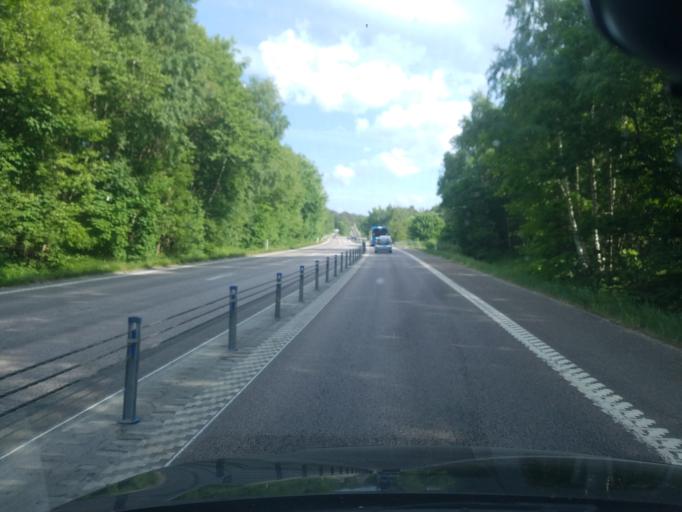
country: SE
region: Vaestra Goetaland
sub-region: Goteborg
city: Billdal
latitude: 57.6117
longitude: 11.9433
